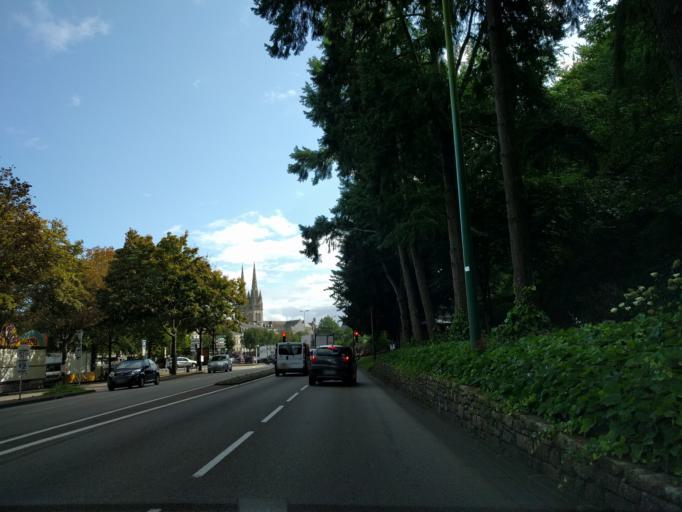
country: FR
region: Brittany
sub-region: Departement du Finistere
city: Quimper
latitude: 47.9928
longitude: -4.1066
